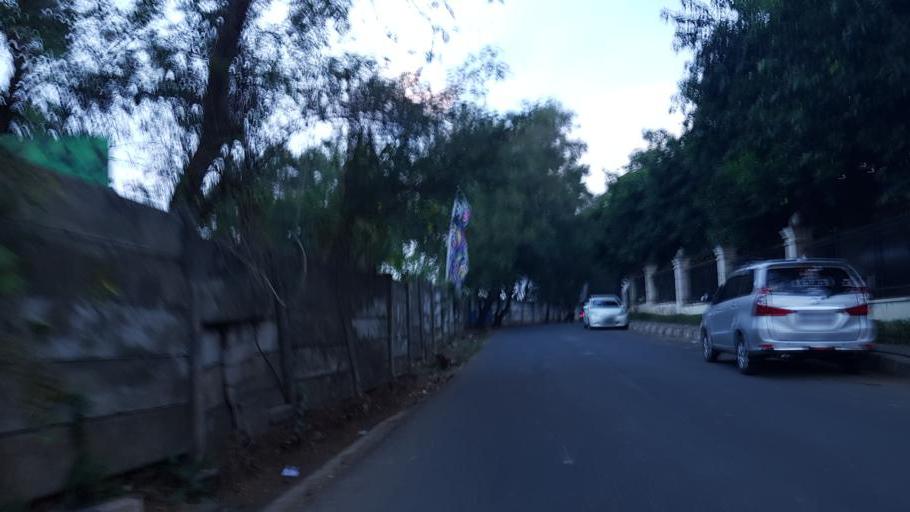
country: ID
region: West Java
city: Pamulang
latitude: -6.2935
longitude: 106.7977
